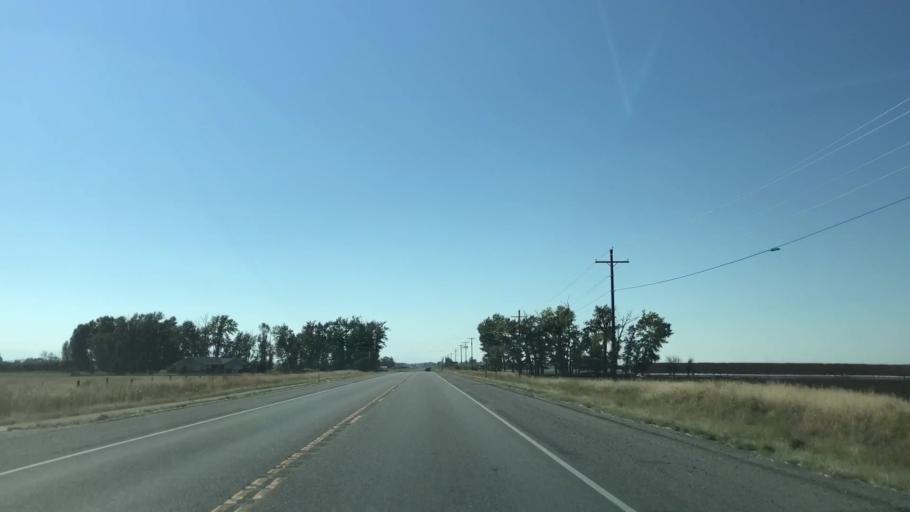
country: US
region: Montana
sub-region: Gallatin County
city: Belgrade
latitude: 45.7293
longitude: -111.1654
